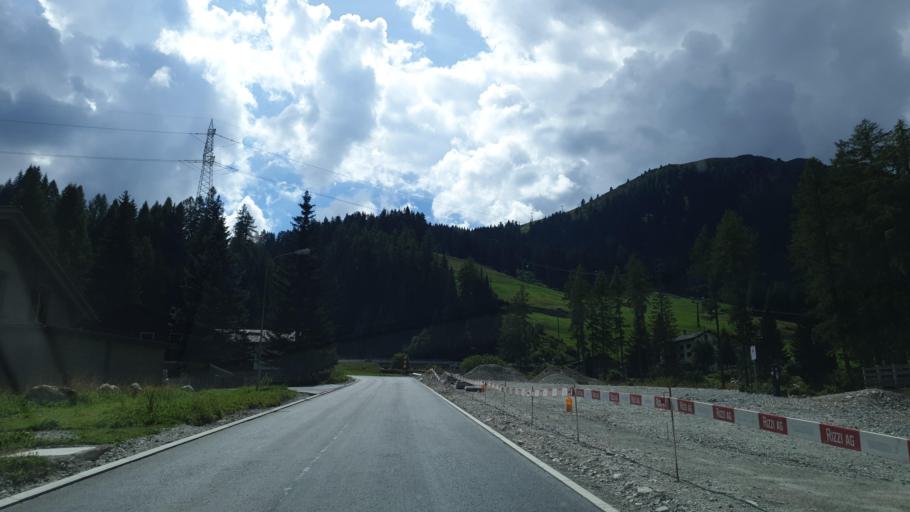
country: CH
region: Grisons
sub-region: Hinterrhein District
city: Hinterrhein
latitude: 46.5496
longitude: 9.3233
